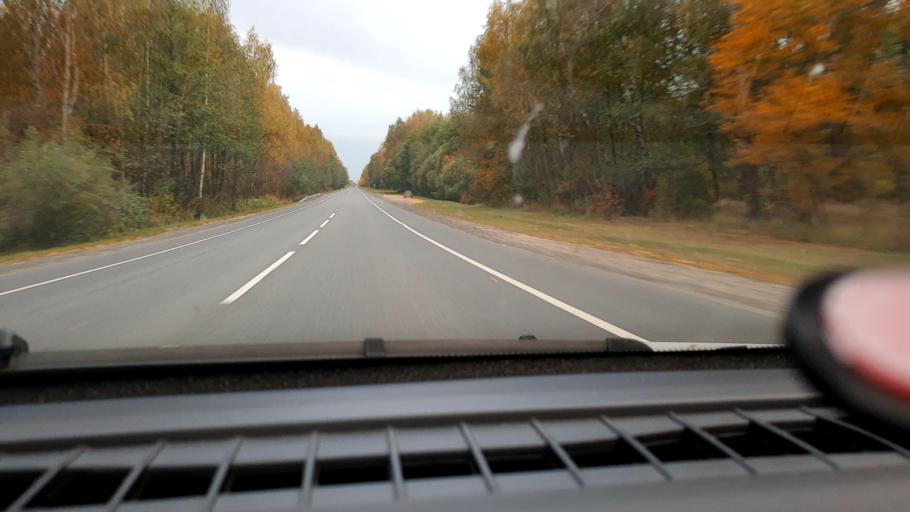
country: RU
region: Vladimir
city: Orgtrud
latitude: 56.2013
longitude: 40.7918
